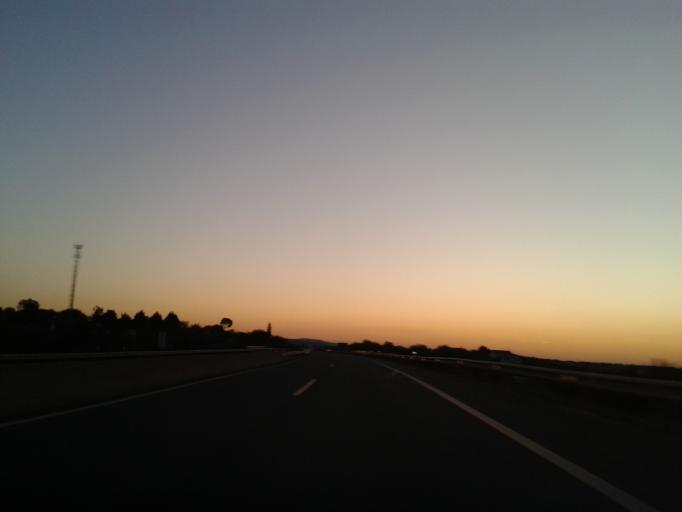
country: PT
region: Faro
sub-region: Albufeira
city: Ferreiras
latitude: 37.1358
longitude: -8.2488
